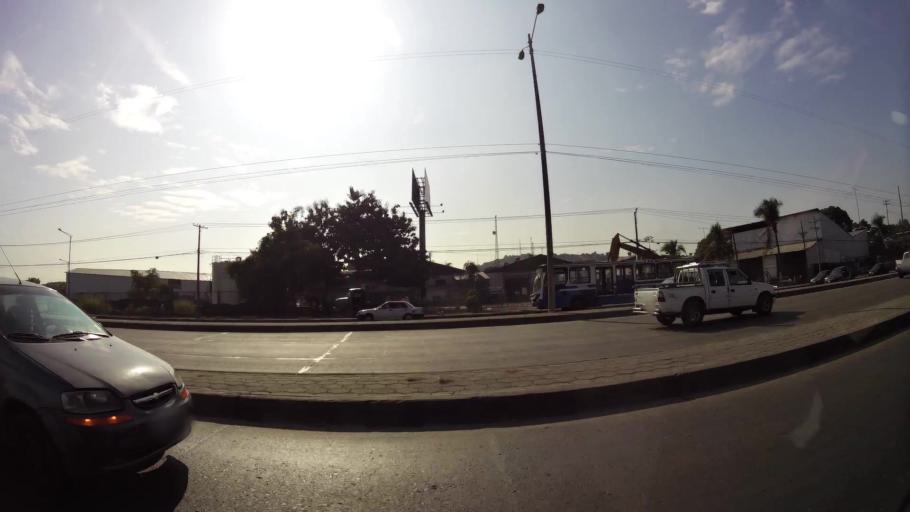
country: EC
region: Guayas
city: Santa Lucia
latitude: -2.0810
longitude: -79.9395
